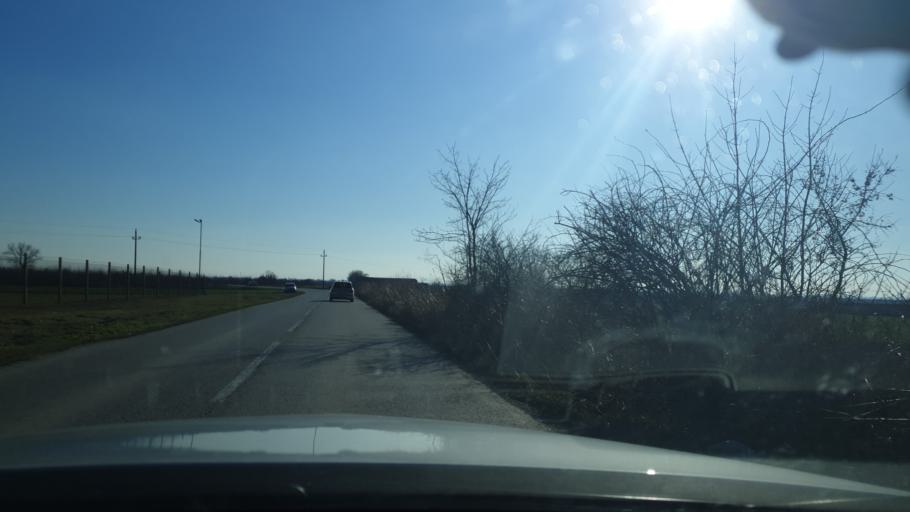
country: RS
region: Autonomna Pokrajina Vojvodina
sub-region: Sremski Okrug
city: Ruma
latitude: 45.0444
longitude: 19.8048
